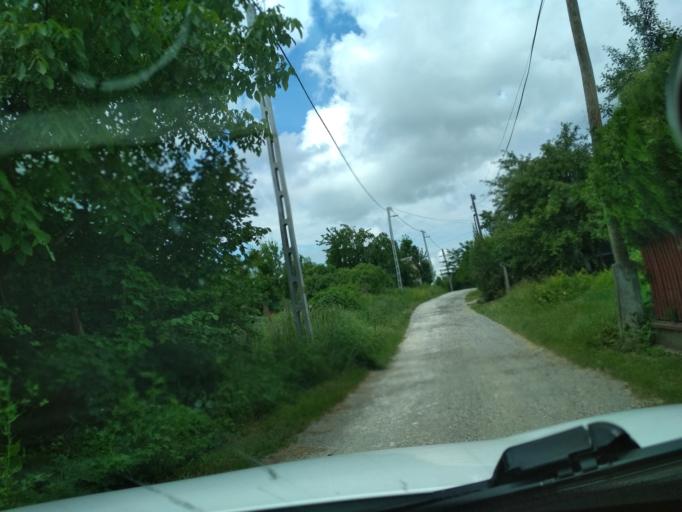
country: HU
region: Jasz-Nagykun-Szolnok
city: Tiszafured
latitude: 47.6072
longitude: 20.7463
